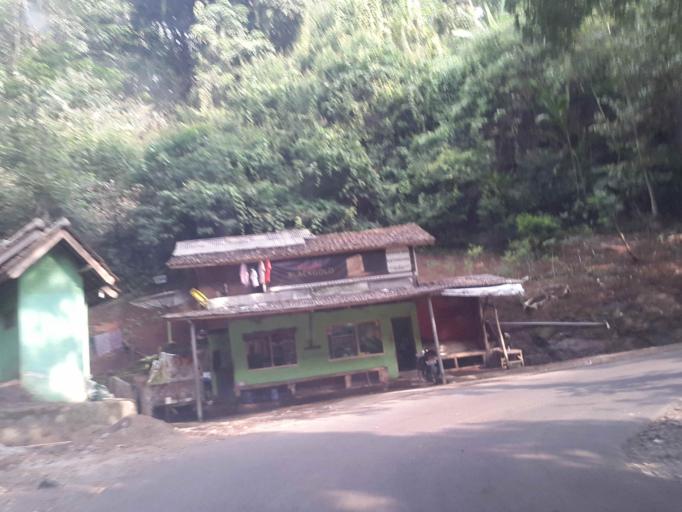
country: ID
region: West Java
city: Ciranjang-hilir
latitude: -6.7347
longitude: 107.1959
